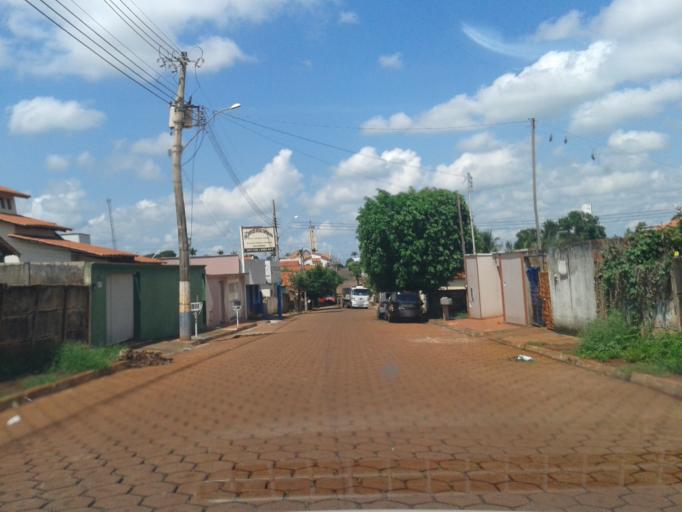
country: BR
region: Minas Gerais
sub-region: Centralina
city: Centralina
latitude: -18.5838
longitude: -49.1952
